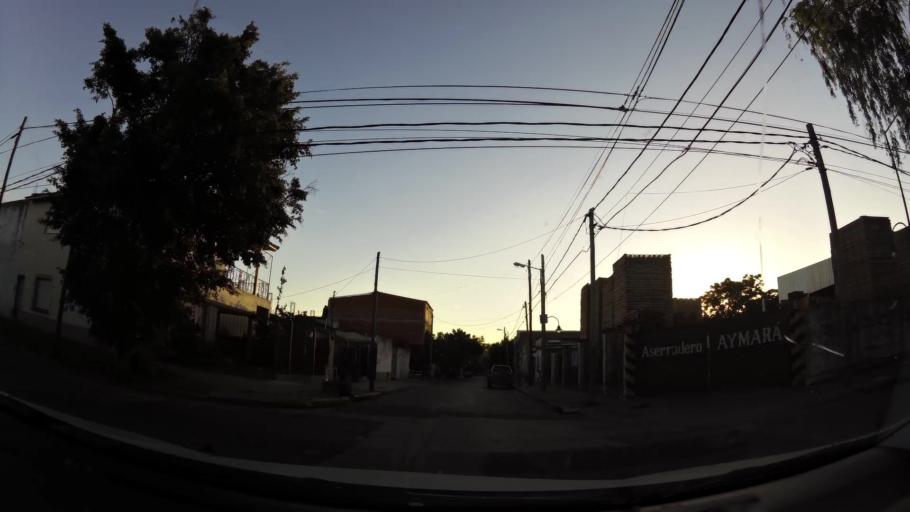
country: AR
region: Buenos Aires
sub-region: Partido de Tigre
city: Tigre
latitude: -34.4409
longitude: -58.5710
